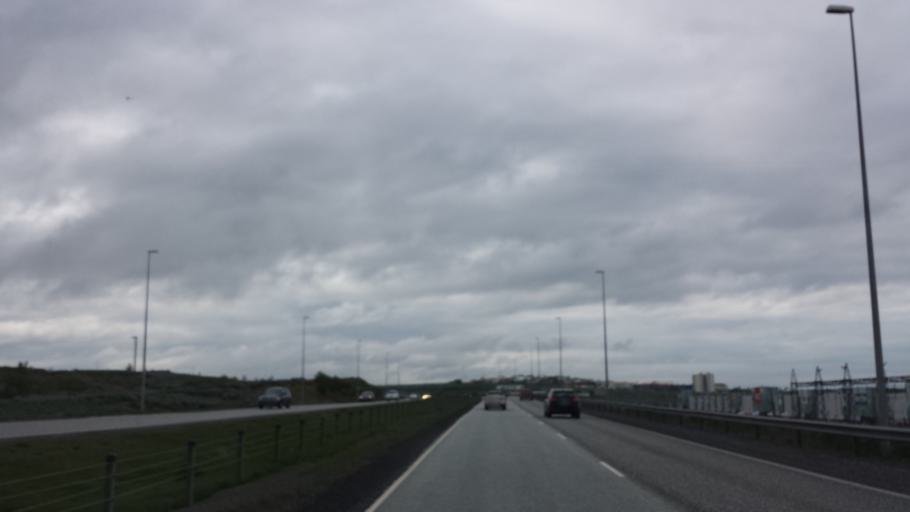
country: IS
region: Capital Region
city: Mosfellsbaer
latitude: 64.1475
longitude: -21.7475
